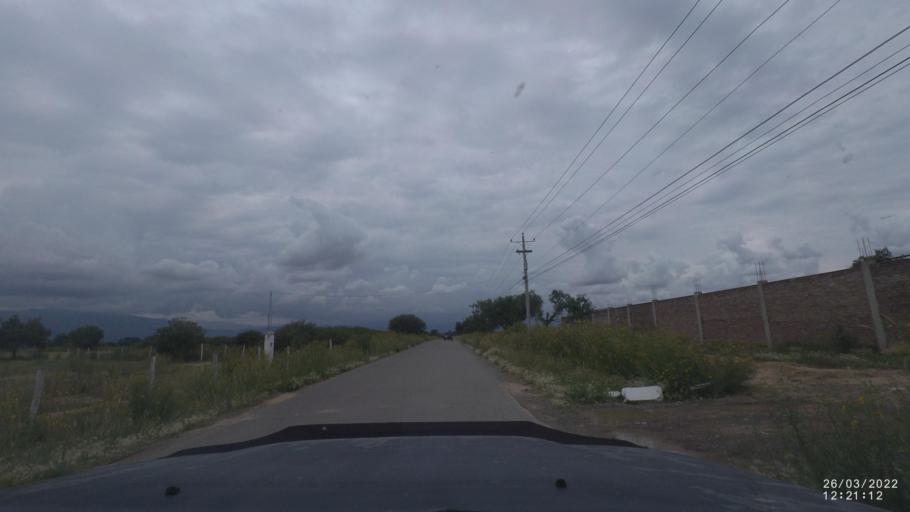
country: BO
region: Cochabamba
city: Cliza
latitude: -17.6003
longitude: -65.9682
